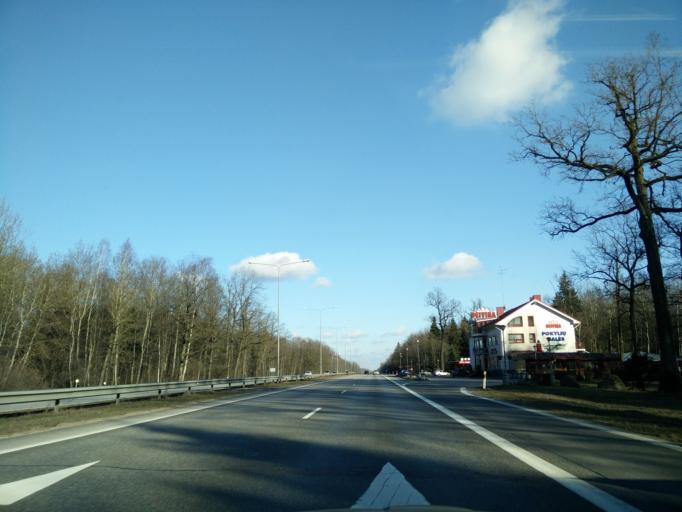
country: LT
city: Ramuciai
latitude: 54.9297
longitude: 24.0143
